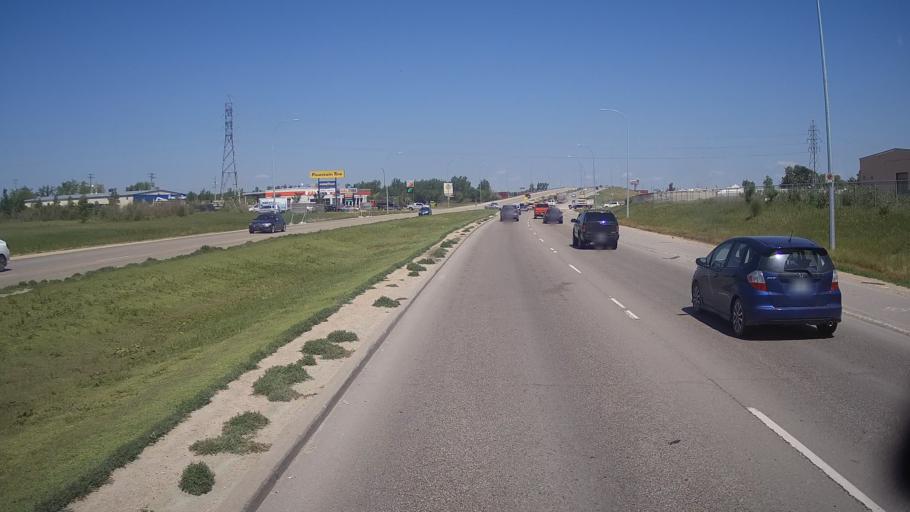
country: CA
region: Manitoba
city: Winnipeg
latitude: 49.8891
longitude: -97.0722
